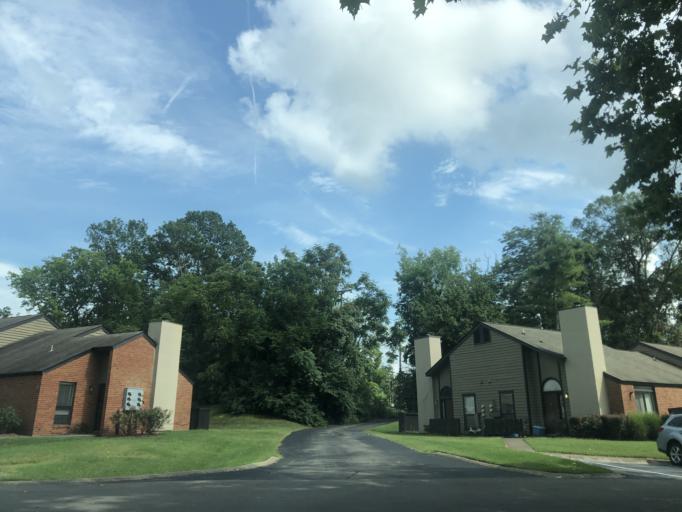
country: US
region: Tennessee
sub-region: Davidson County
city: Lakewood
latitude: 36.1626
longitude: -86.6289
